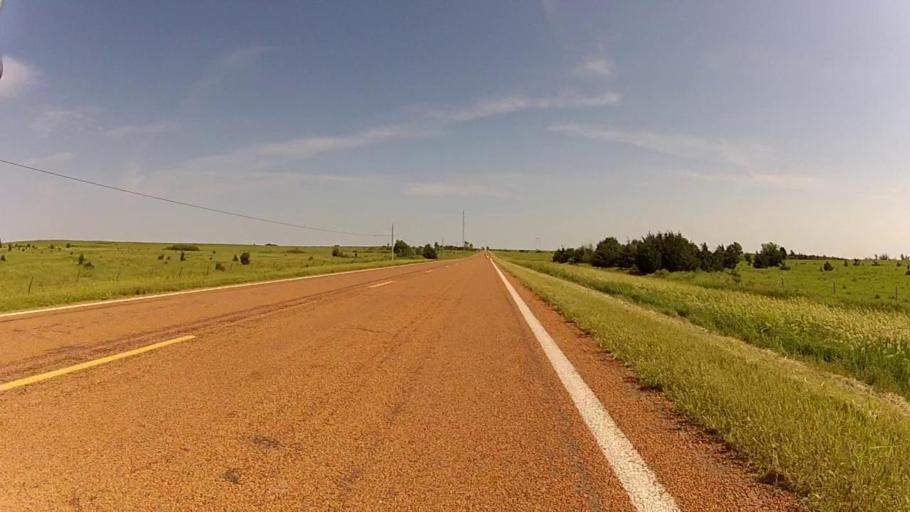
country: US
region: Kansas
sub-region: Cowley County
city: Winfield
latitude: 37.1027
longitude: -96.6436
